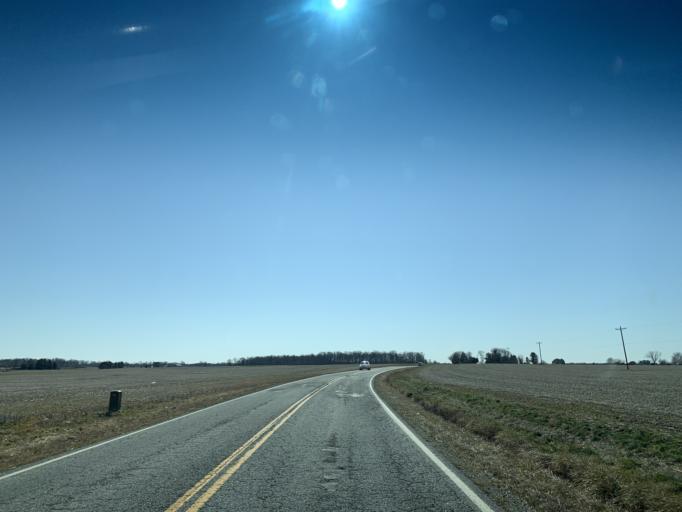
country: US
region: Maryland
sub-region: Cecil County
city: Charlestown
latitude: 39.4420
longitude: -75.9043
